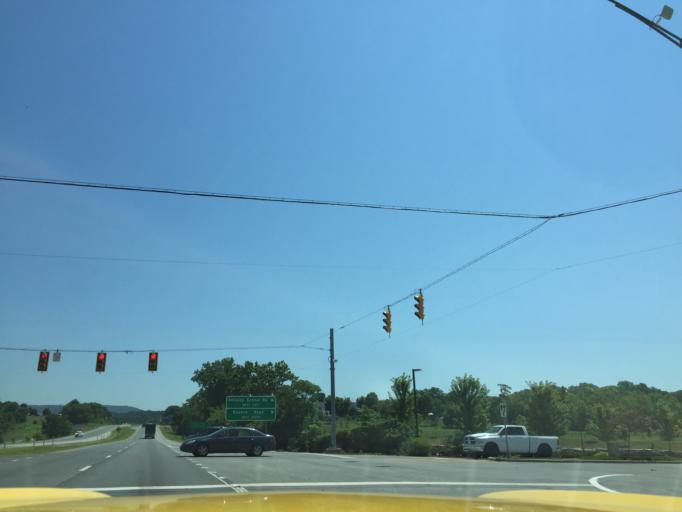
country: US
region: West Virginia
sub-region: Jefferson County
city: Bolivar
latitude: 39.3154
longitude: -77.7867
